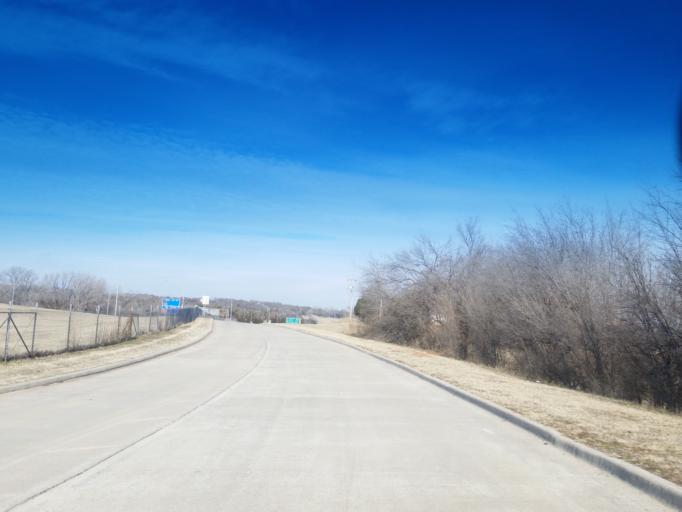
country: US
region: Oklahoma
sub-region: Oklahoma County
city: Edmond
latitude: 35.6134
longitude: -97.4238
